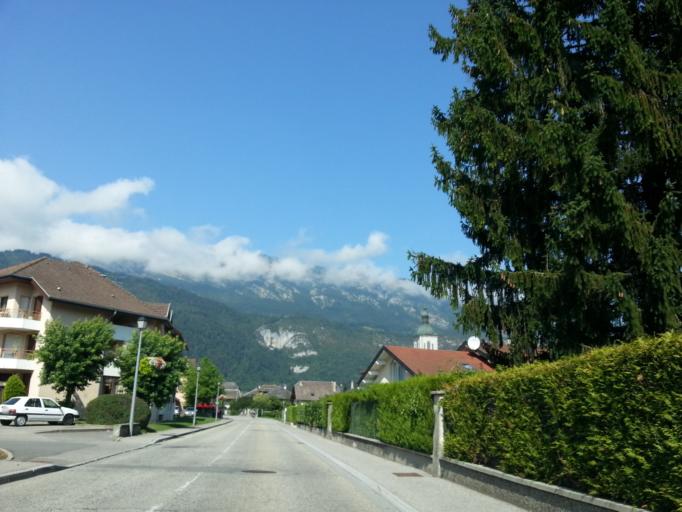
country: FR
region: Rhone-Alpes
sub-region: Departement de la Haute-Savoie
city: Doussard
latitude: 45.7755
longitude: 6.2237
